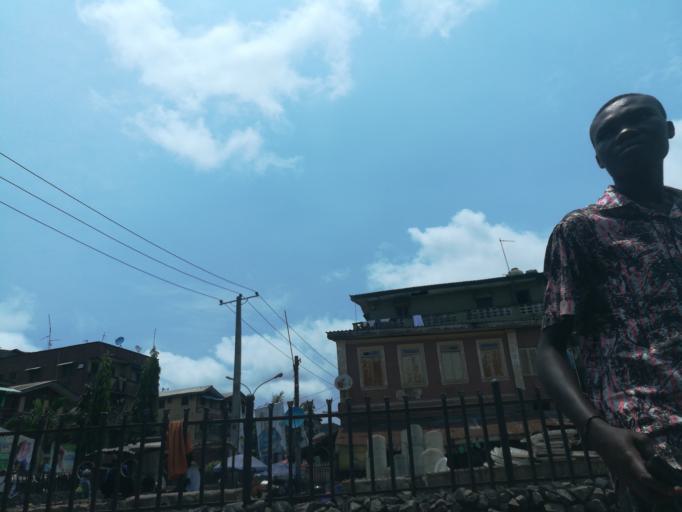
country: NG
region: Lagos
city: Lagos
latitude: 6.4527
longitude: 3.3985
